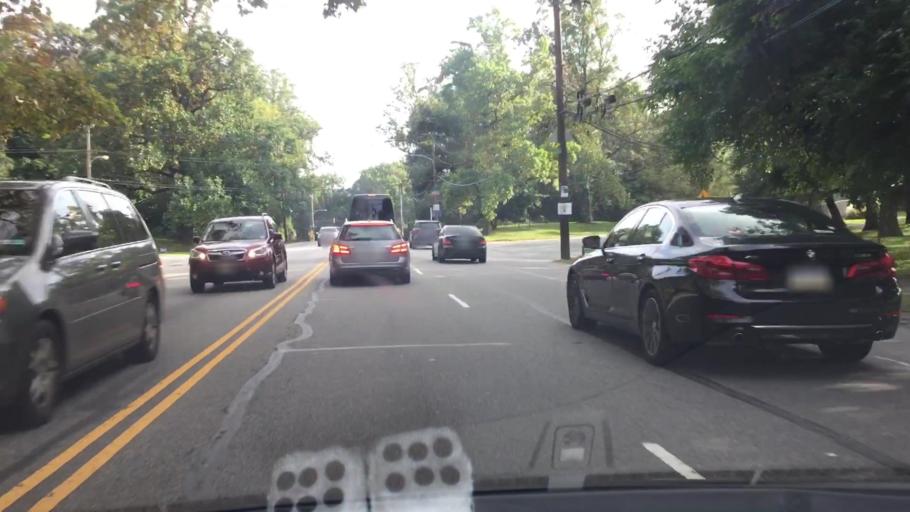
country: US
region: Pennsylvania
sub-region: Montgomery County
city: Bala-Cynwyd
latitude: 39.9948
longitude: -75.2182
